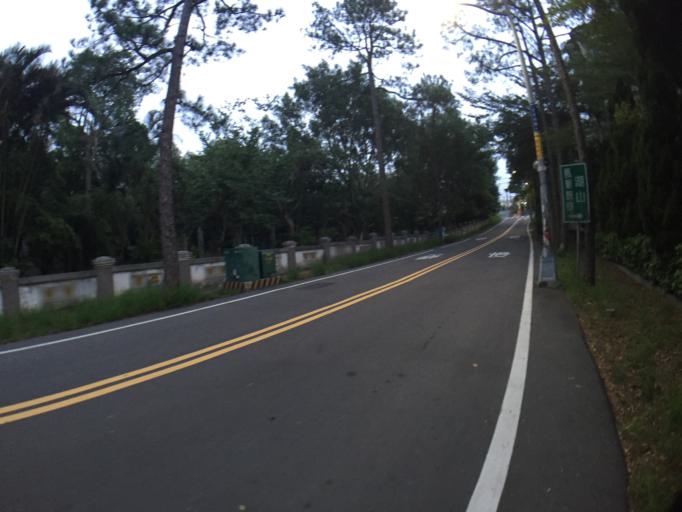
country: TW
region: Taiwan
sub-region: Hsinchu
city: Hsinchu
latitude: 24.7720
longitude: 120.9716
